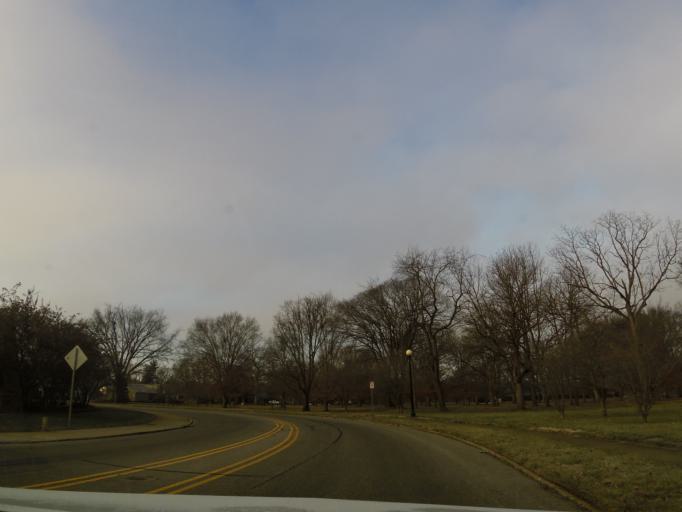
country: US
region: Indiana
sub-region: Bartholomew County
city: Columbus
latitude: 39.2298
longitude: -85.9116
